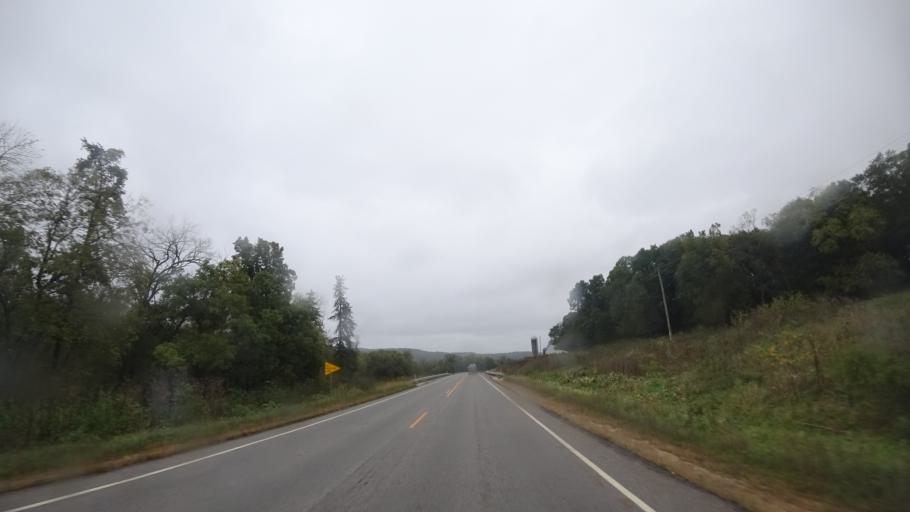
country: US
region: Wisconsin
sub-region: Crawford County
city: Prairie du Chien
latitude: 43.0375
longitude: -90.9881
